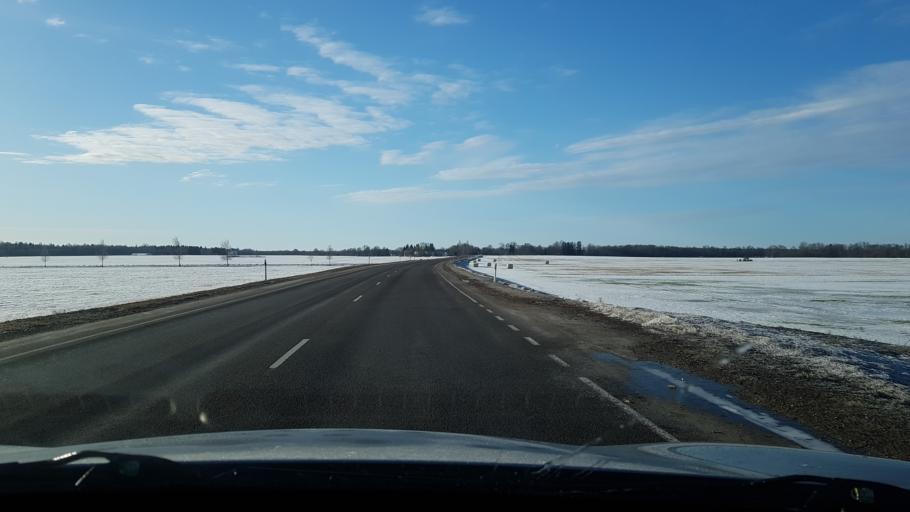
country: EE
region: Jogevamaa
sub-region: Poltsamaa linn
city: Poltsamaa
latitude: 58.7234
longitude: 25.7626
